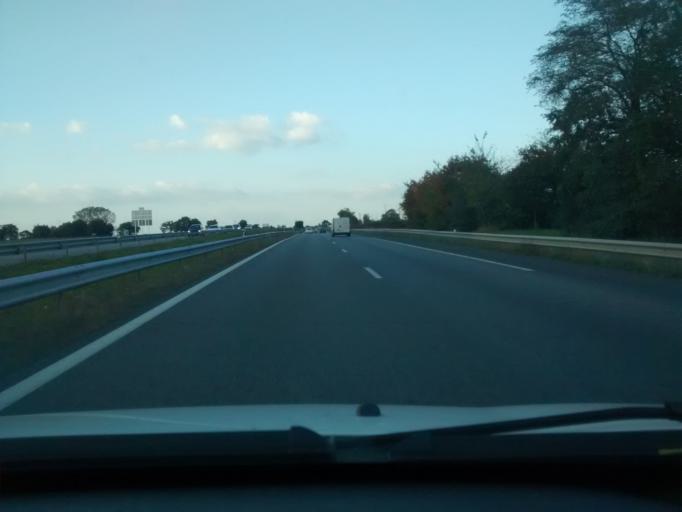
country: FR
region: Brittany
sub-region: Departement d'Ille-et-Vilaine
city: Pance
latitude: 47.8989
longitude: -1.6861
